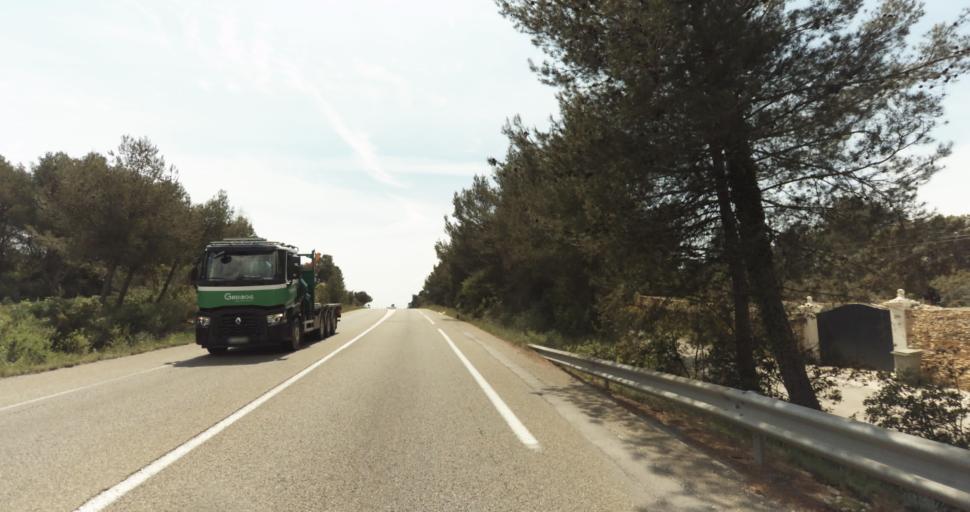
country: FR
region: Languedoc-Roussillon
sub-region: Departement du Gard
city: Nimes
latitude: 43.8623
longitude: 4.3234
